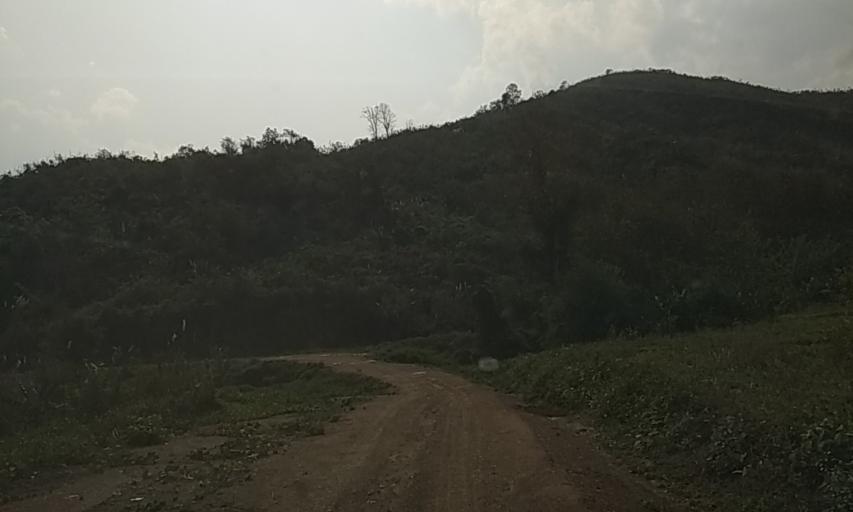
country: LA
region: Louangphabang
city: Louangphabang
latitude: 20.0552
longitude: 101.8577
